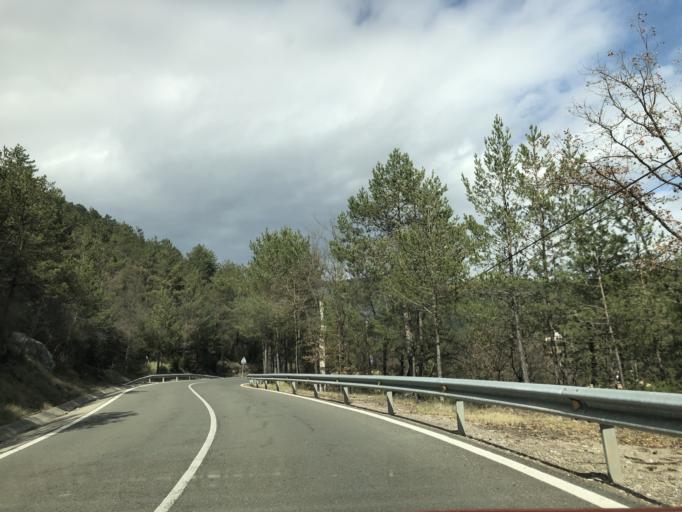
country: ES
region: Catalonia
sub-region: Provincia de Barcelona
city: Capolat
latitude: 42.1265
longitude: 1.6629
